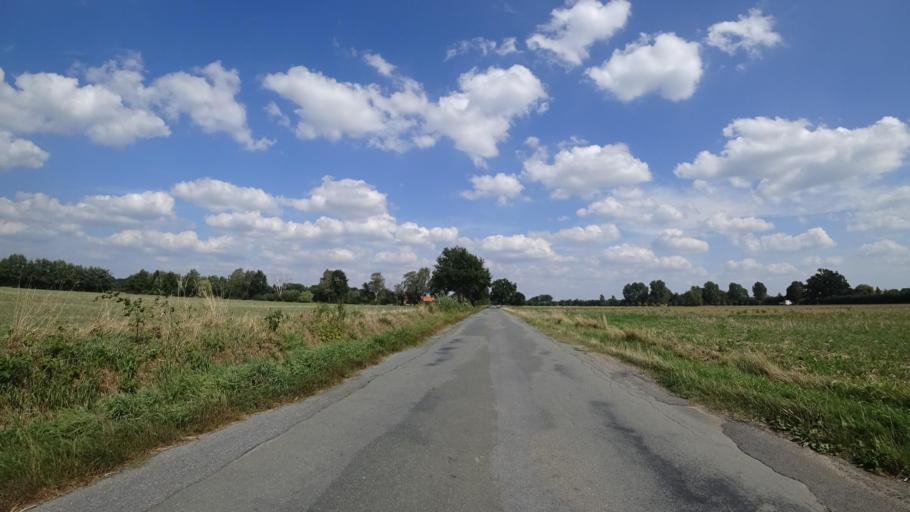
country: DE
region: North Rhine-Westphalia
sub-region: Regierungsbezirk Detmold
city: Rheda-Wiedenbruck
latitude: 51.8729
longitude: 8.2785
